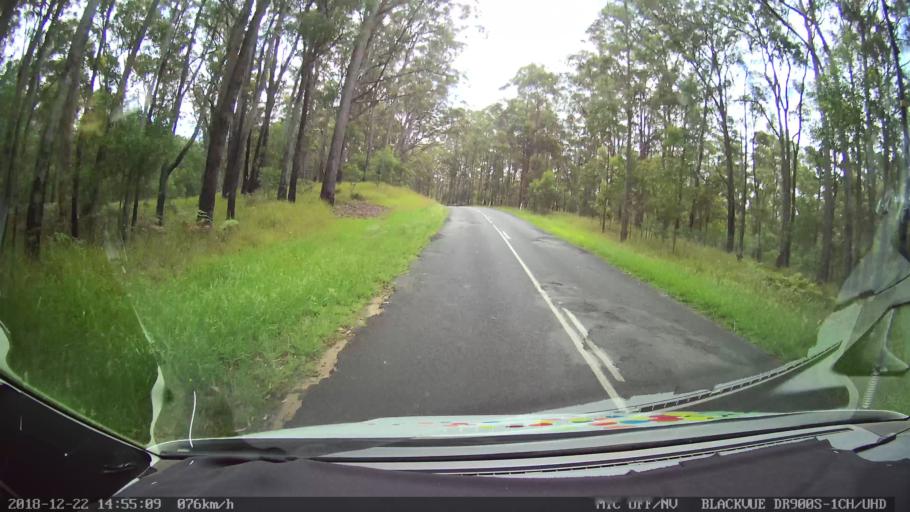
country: AU
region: New South Wales
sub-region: Bellingen
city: Dorrigo
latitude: -30.2290
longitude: 152.5248
